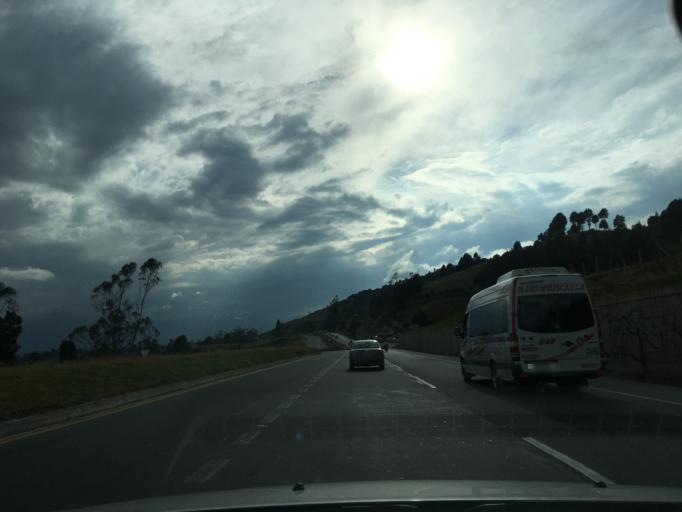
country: CO
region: Boyaca
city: Tunja
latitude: 5.4703
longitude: -73.4101
